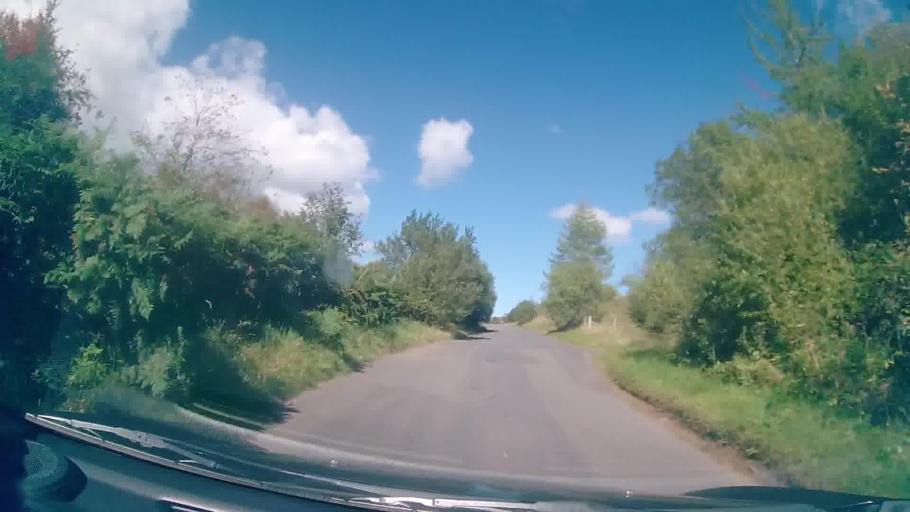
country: GB
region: Wales
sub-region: Merthyr Tydfil County Borough
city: Merthyr Tydfil
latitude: 51.8407
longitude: -3.3818
